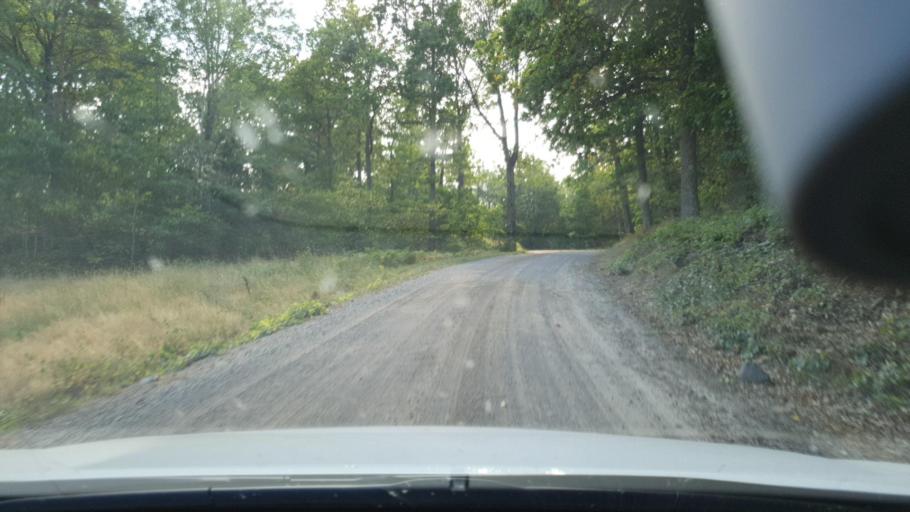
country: SE
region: Kalmar
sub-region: Vasterviks Kommun
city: Ankarsrum
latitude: 57.7007
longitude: 16.4552
